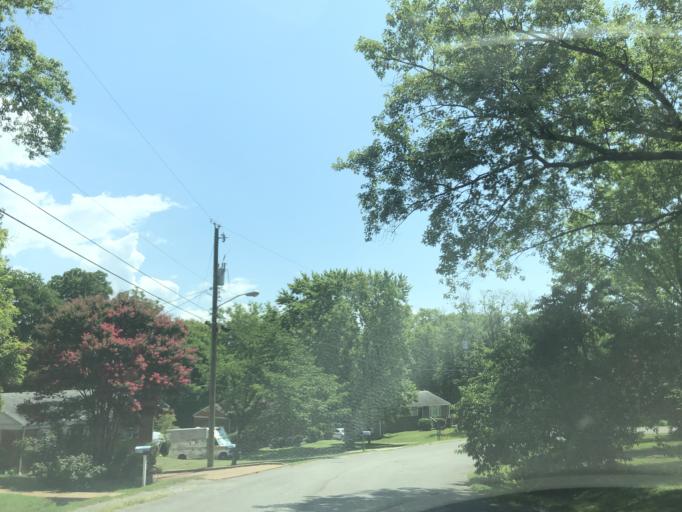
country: US
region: Tennessee
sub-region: Davidson County
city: Lakewood
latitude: 36.1533
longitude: -86.6610
